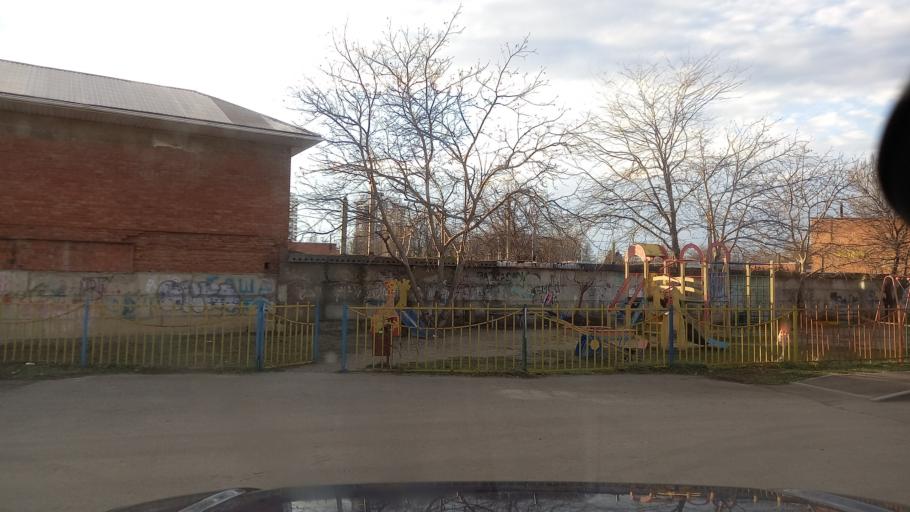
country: RU
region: Krasnodarskiy
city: Pashkovskiy
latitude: 45.0113
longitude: 39.1067
